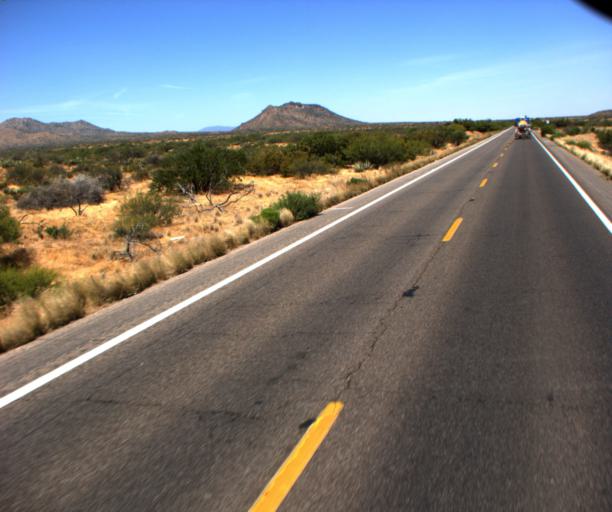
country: US
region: Arizona
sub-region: Gila County
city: Peridot
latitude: 33.3165
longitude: -110.5238
